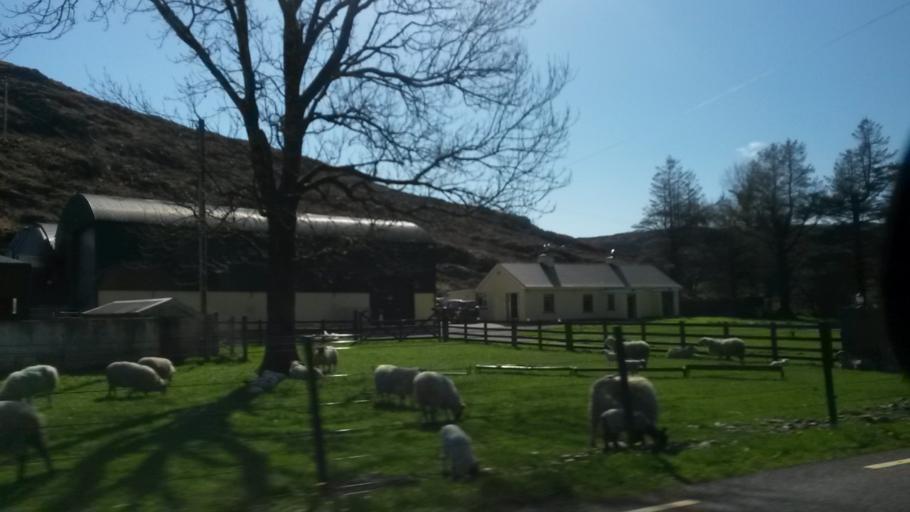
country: IE
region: Munster
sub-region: Ciarrai
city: Cill Airne
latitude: 51.9296
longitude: -9.3834
